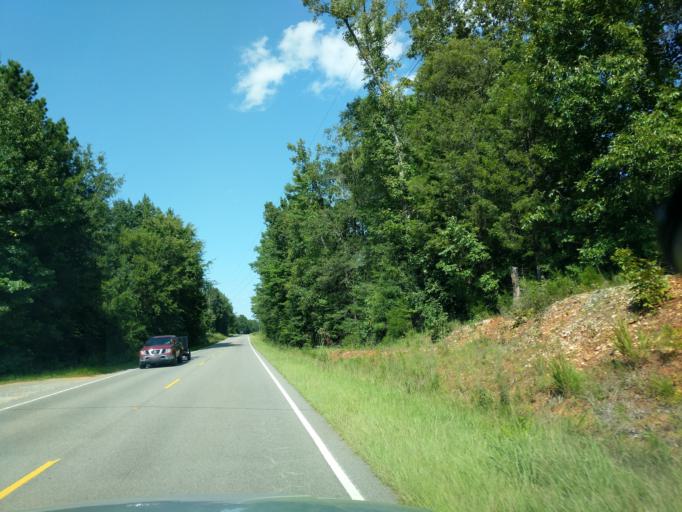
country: US
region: South Carolina
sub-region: Newberry County
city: Prosperity
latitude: 34.1106
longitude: -81.5624
